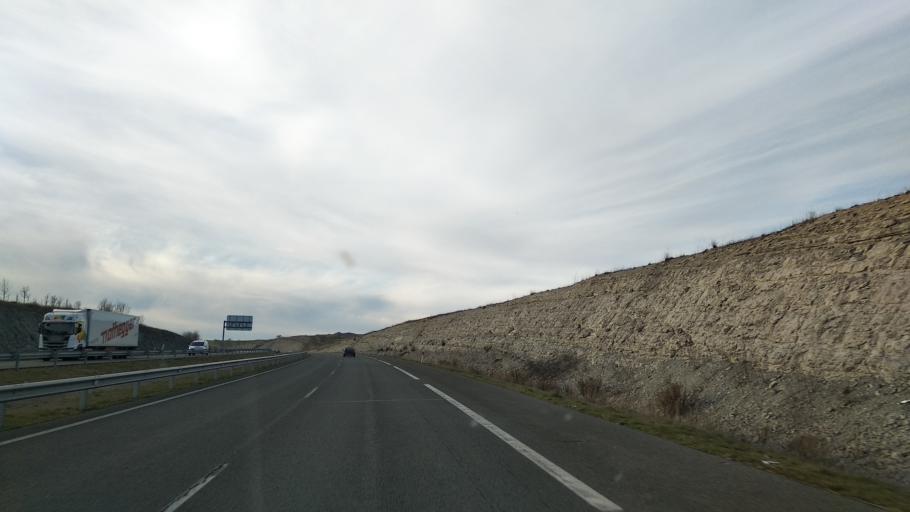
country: ES
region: Basque Country
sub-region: Provincia de Alava
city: Salvatierra
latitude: 42.8563
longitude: -2.4311
